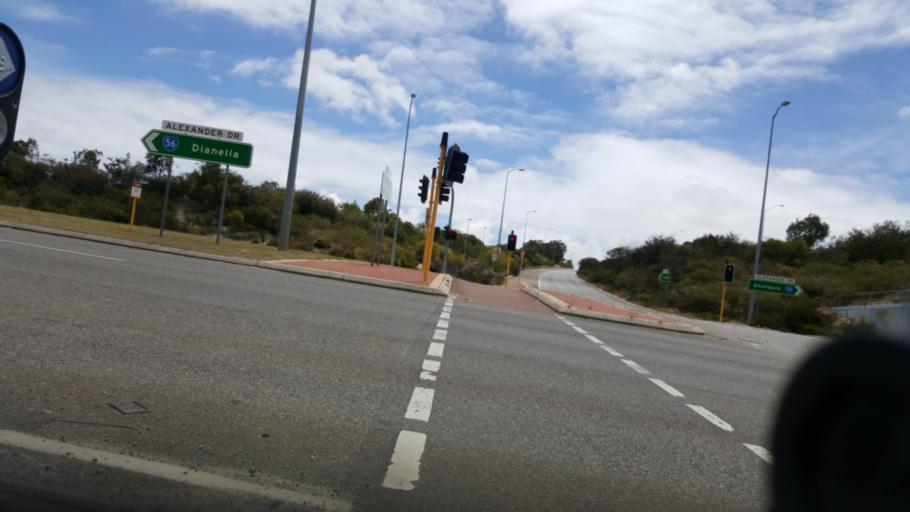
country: AU
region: Western Australia
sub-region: Stirling
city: Westminster
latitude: -31.8686
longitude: 115.8782
